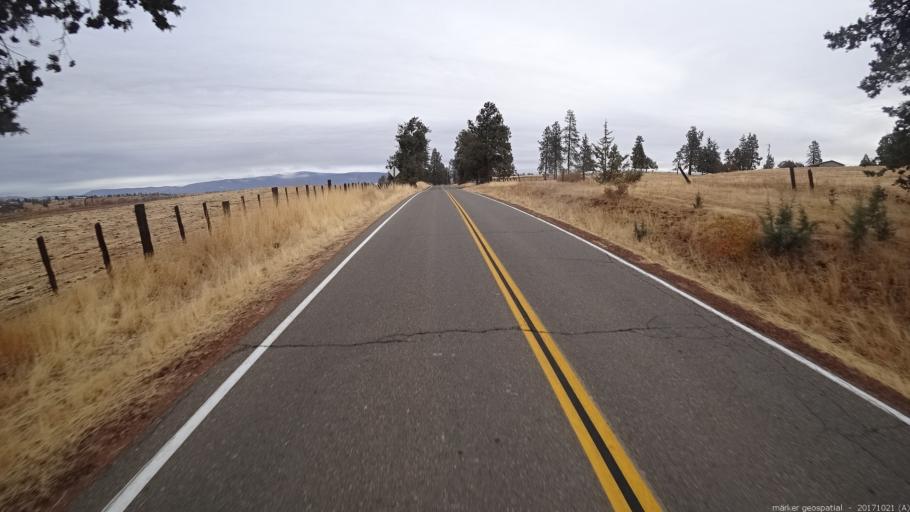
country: US
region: California
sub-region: Shasta County
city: Burney
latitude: 41.0131
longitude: -121.4198
